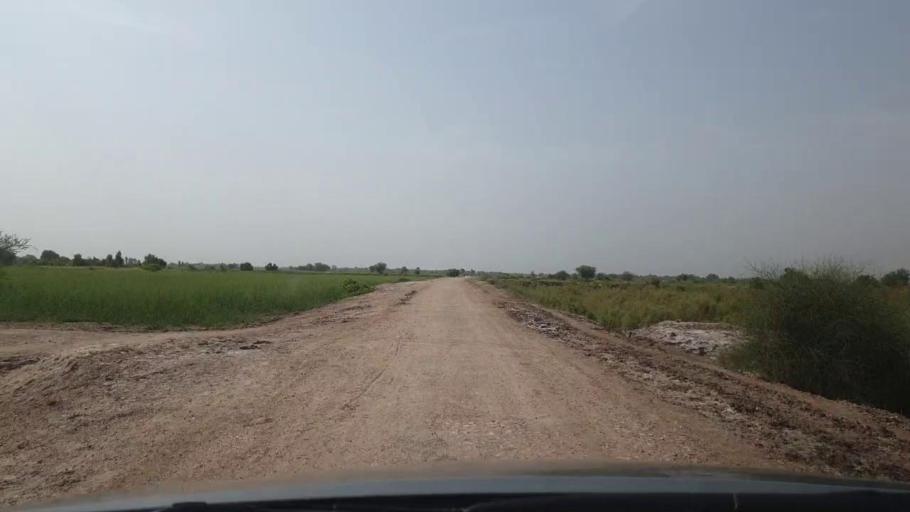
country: PK
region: Sindh
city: Rohri
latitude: 27.6741
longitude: 69.0126
